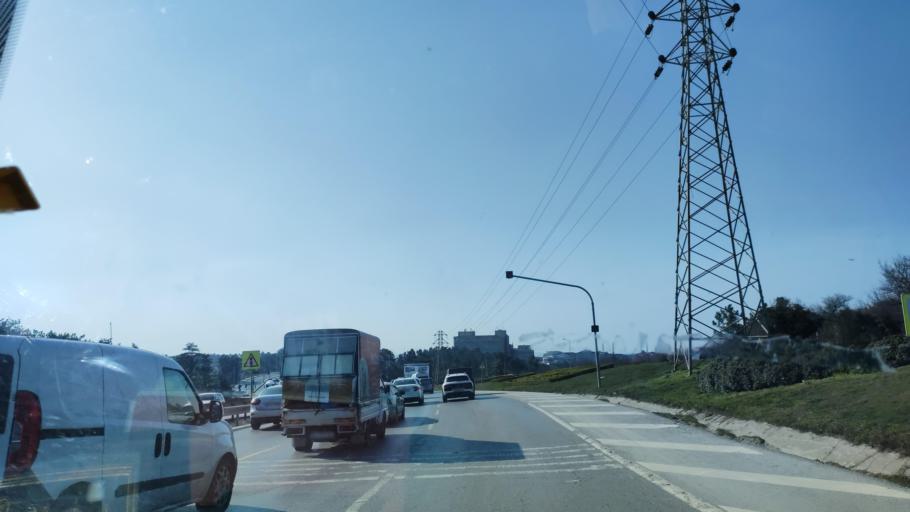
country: TR
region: Istanbul
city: Basaksehir
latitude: 41.1736
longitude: 28.7558
